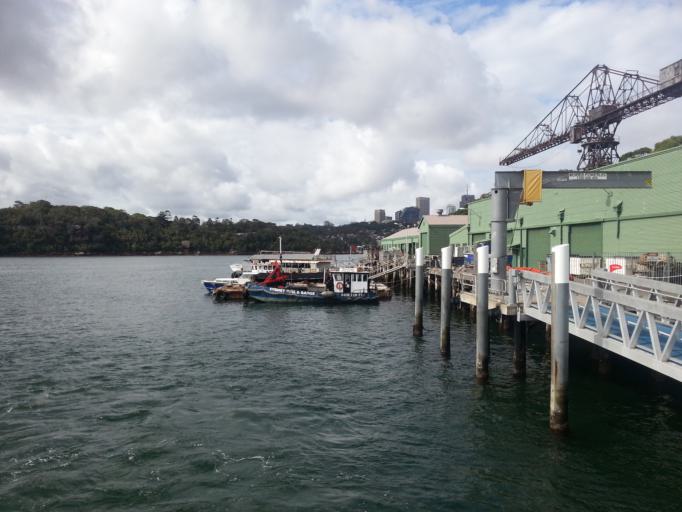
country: AU
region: New South Wales
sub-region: Leichhardt
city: Balmain East
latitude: -33.8531
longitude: 151.1947
